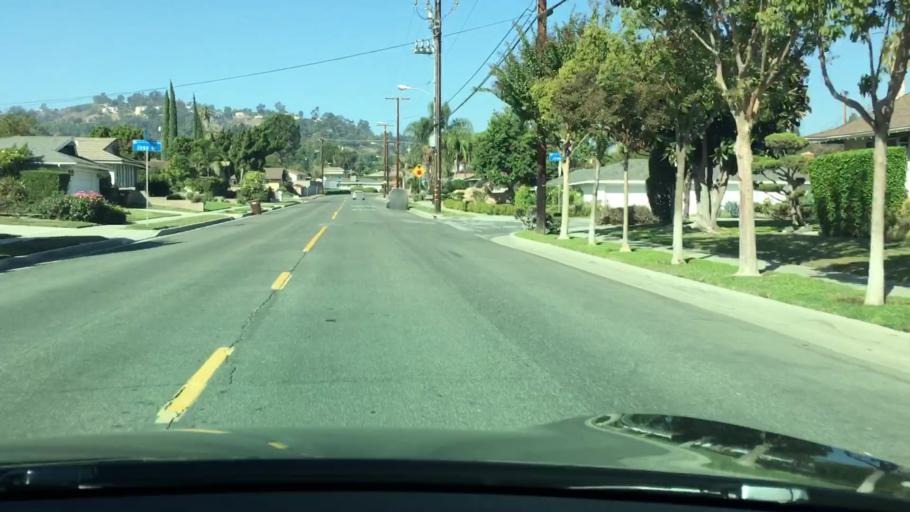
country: US
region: California
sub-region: Los Angeles County
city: Hacienda Heights
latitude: 33.9952
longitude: -117.9760
